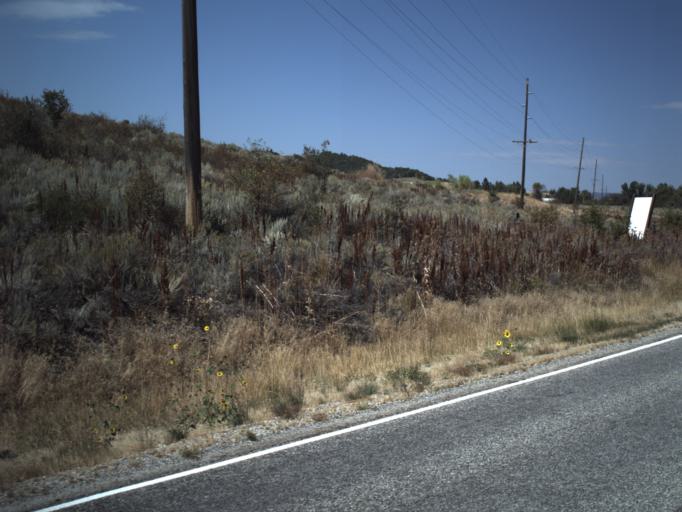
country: US
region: Utah
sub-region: Weber County
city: Wolf Creek
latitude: 41.2784
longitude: -111.8205
